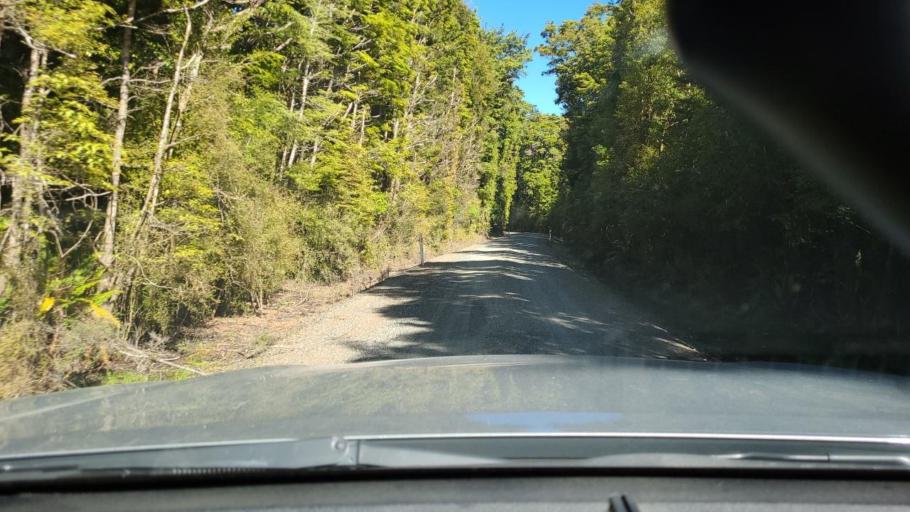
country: NZ
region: Southland
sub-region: Southland District
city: Te Anau
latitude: -45.9904
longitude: 167.3870
